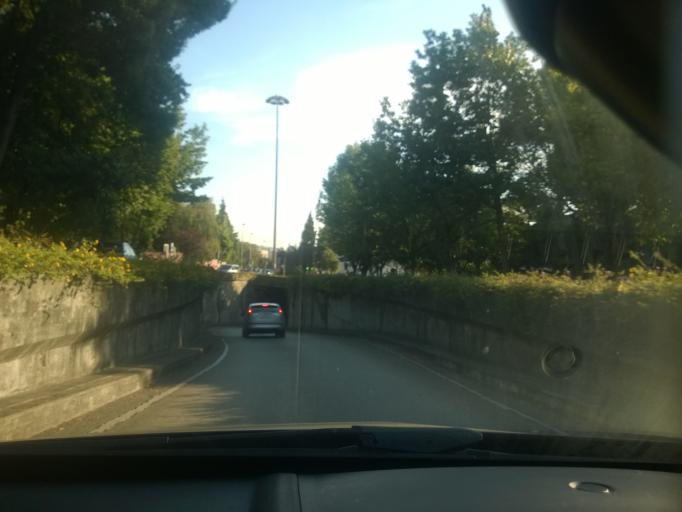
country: PT
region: Porto
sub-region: Porto
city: Porto
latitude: 41.1530
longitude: -8.6323
